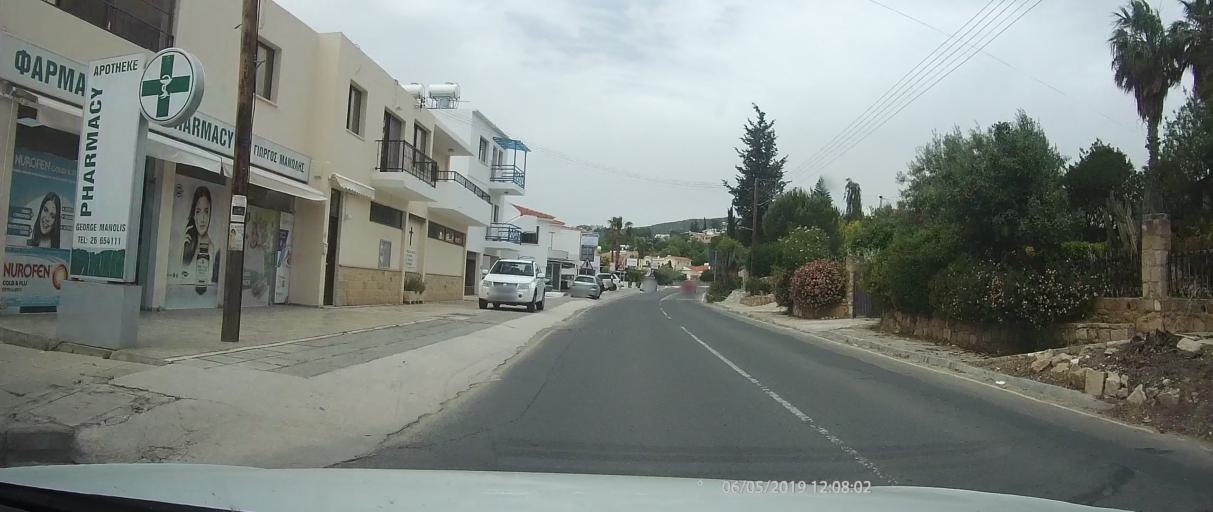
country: CY
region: Pafos
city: Tala
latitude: 34.8317
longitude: 32.4286
